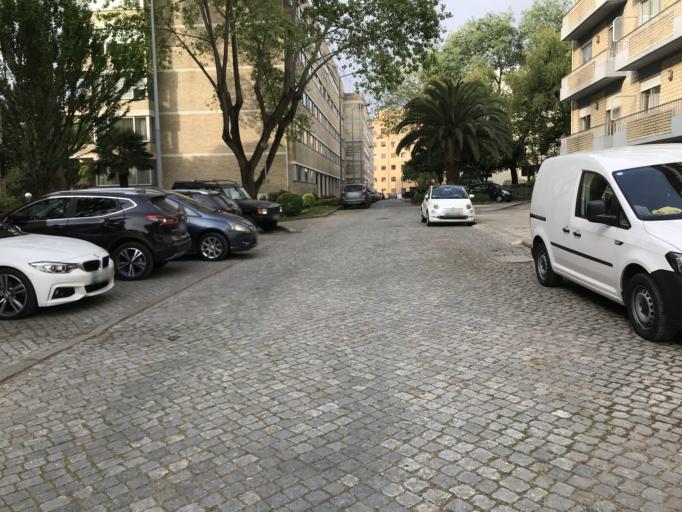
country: PT
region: Porto
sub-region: Matosinhos
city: Senhora da Hora
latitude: 41.1823
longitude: -8.6685
